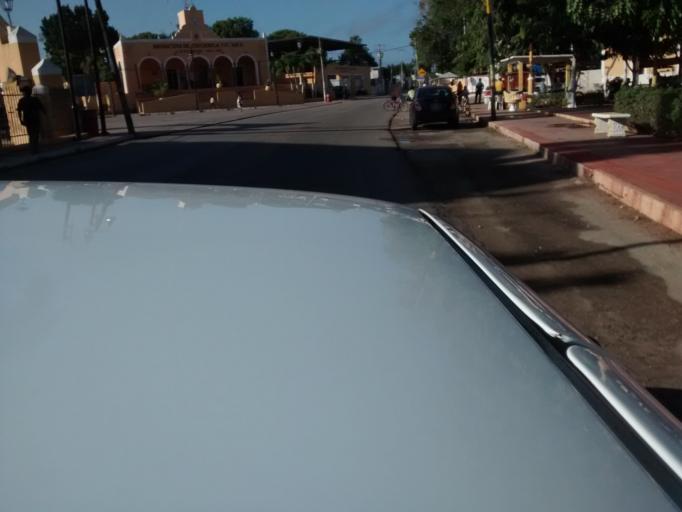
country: MX
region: Yucatan
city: Chichimila
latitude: 20.6318
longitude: -88.2167
